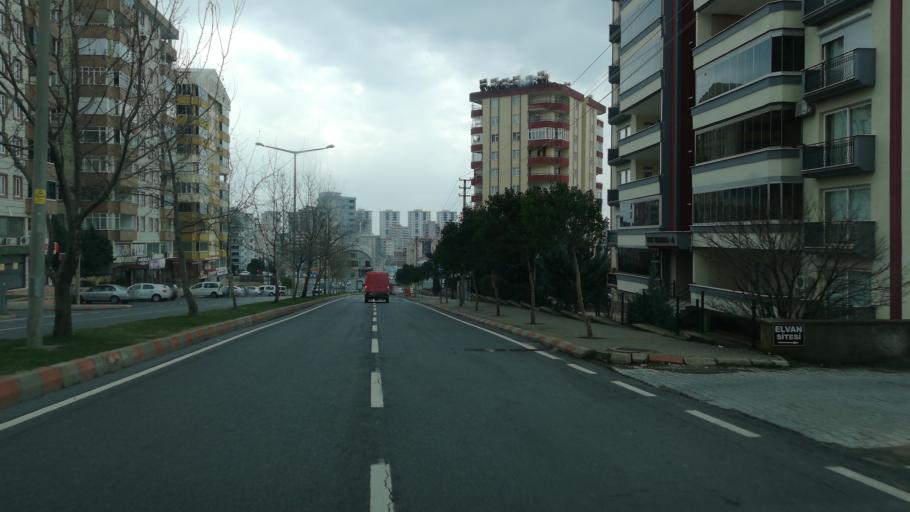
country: TR
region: Kahramanmaras
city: Kahramanmaras
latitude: 37.5848
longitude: 36.8790
